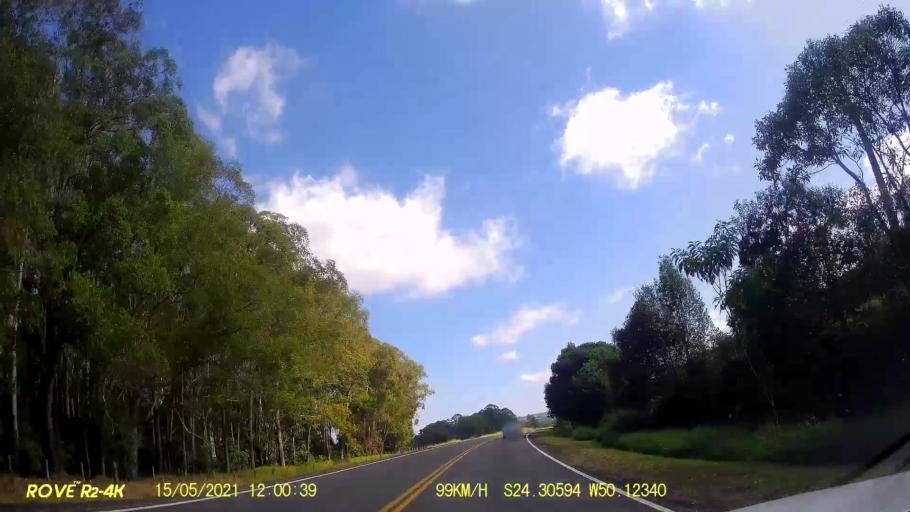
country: BR
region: Parana
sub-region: Pirai Do Sul
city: Pirai do Sul
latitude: -24.3059
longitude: -50.1235
